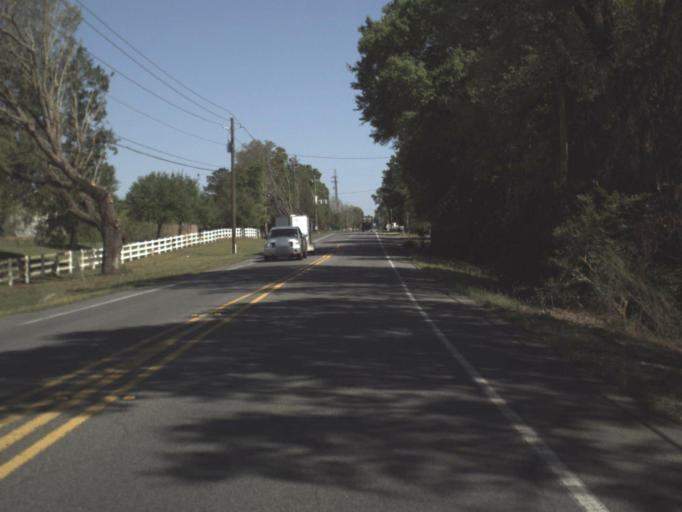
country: US
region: Florida
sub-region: Escambia County
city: Bellview
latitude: 30.5133
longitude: -87.3699
